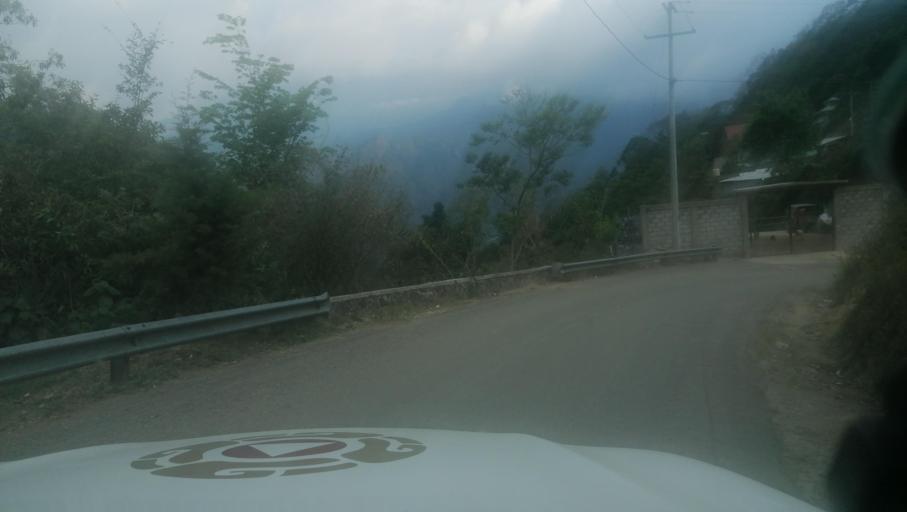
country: MX
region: Chiapas
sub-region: Cacahoatan
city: Benito Juarez
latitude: 15.1731
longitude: -92.1954
